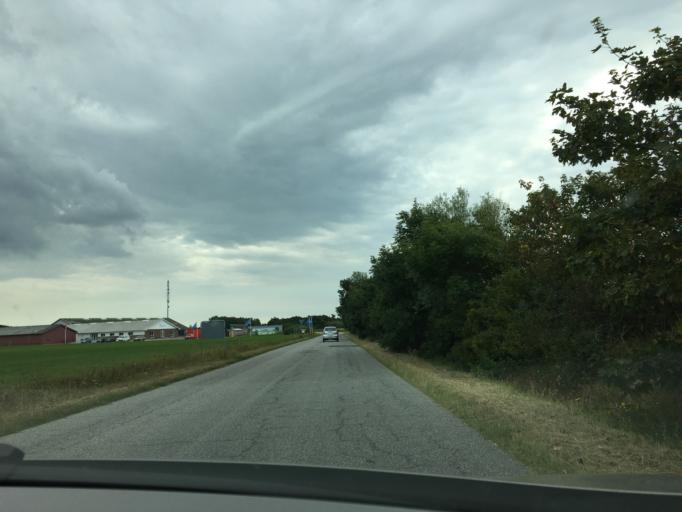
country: DK
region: South Denmark
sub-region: Varde Kommune
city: Oksbol
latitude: 55.8454
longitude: 8.2907
